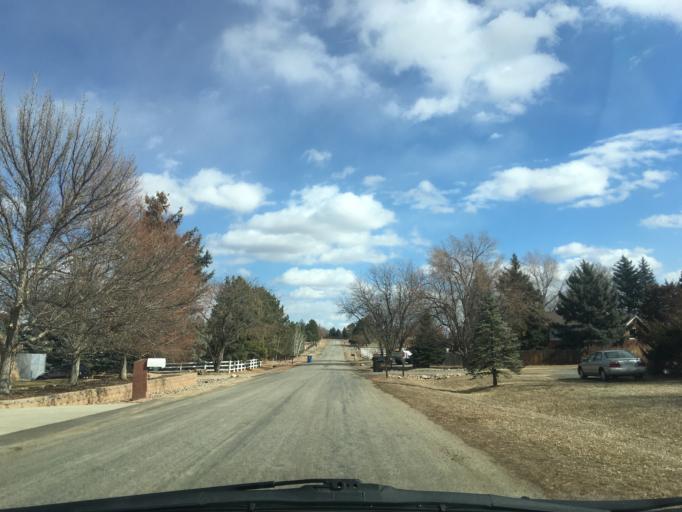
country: US
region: Colorado
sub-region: Boulder County
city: Lafayette
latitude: 39.9600
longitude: -105.0576
